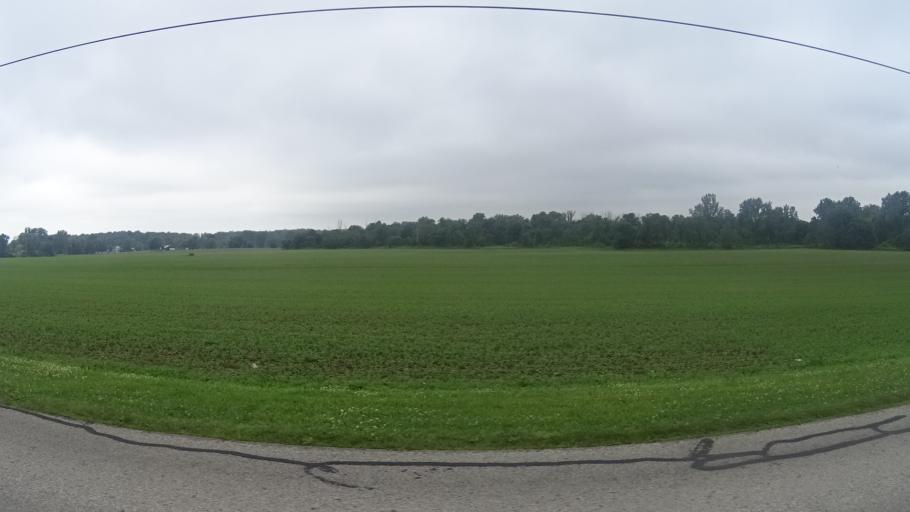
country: US
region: Ohio
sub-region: Erie County
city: Huron
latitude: 41.3177
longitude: -82.4995
